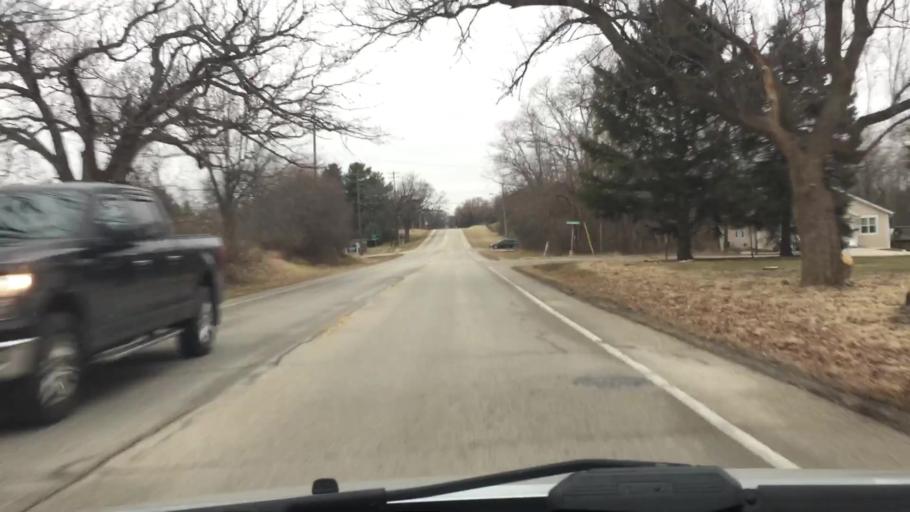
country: US
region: Wisconsin
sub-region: Waukesha County
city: Nashotah
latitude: 43.0828
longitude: -88.4034
